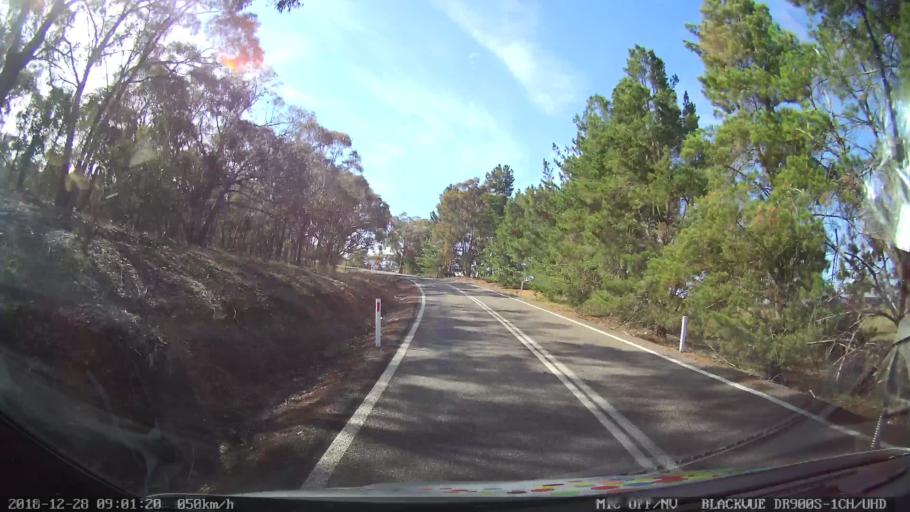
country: AU
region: New South Wales
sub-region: Upper Lachlan Shire
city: Crookwell
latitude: -34.1456
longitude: 149.3332
